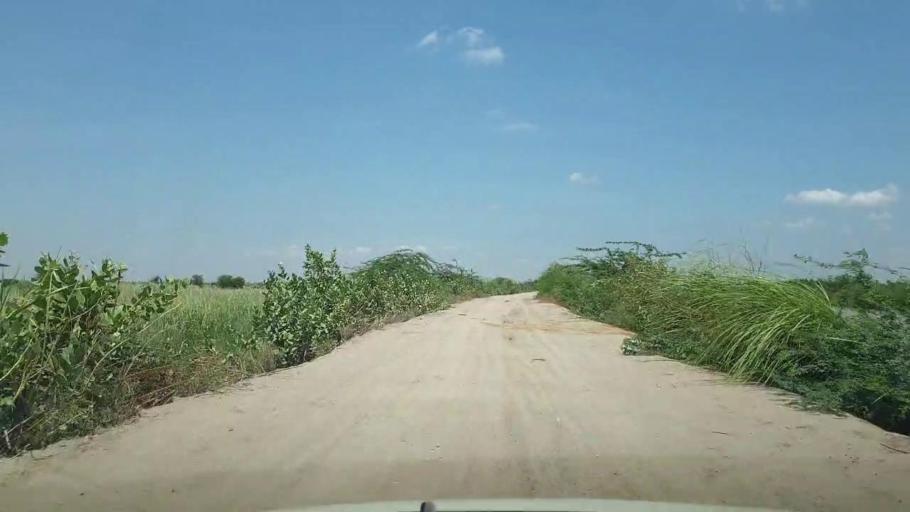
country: PK
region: Sindh
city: Sanghar
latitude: 26.1054
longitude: 69.0059
